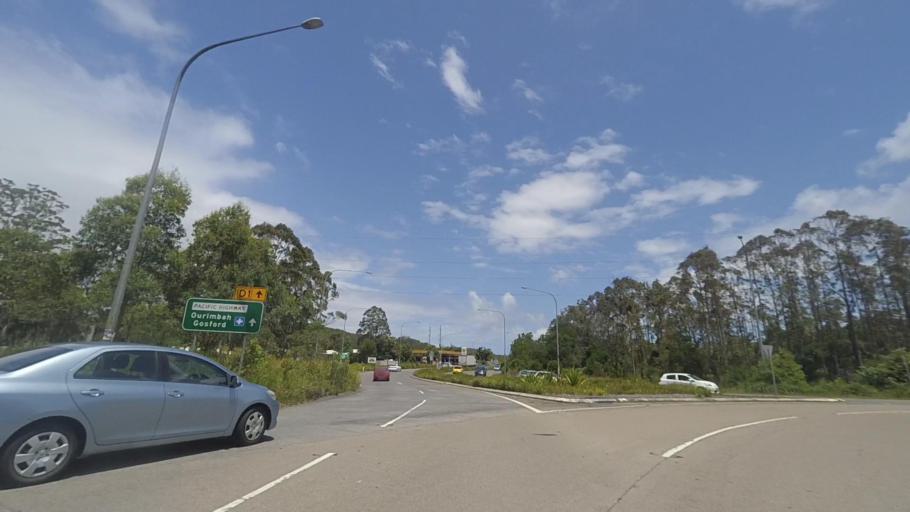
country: AU
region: New South Wales
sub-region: Gosford Shire
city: Lisarow
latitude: -33.3454
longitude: 151.3701
